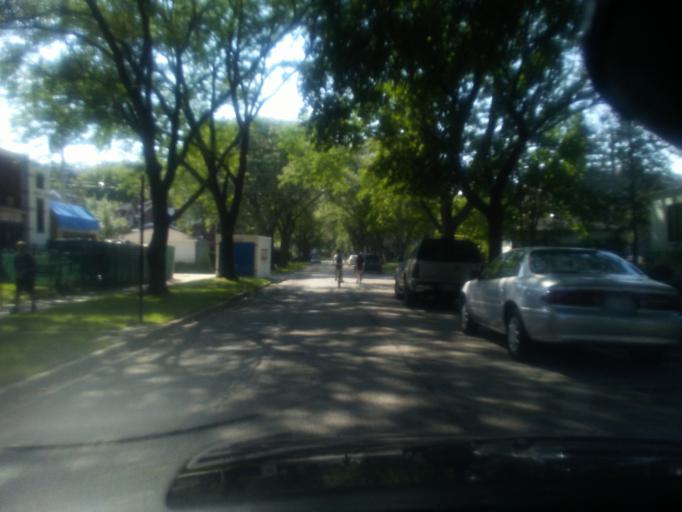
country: US
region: Illinois
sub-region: Cook County
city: Lincolnwood
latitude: 41.9881
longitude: -87.7421
